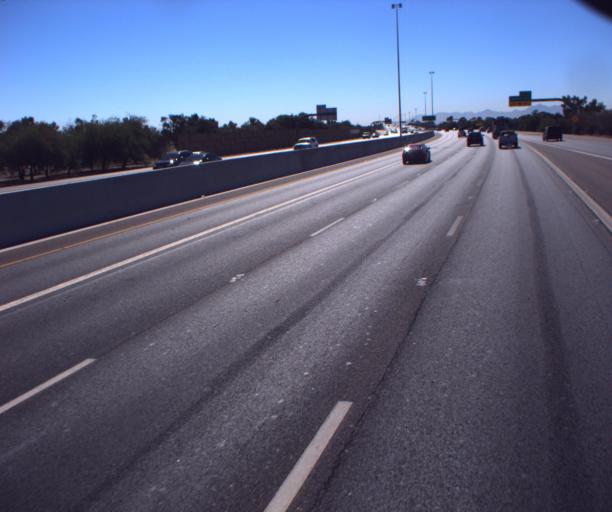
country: US
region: Arizona
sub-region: Maricopa County
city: Sun City
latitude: 33.5899
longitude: -112.2613
